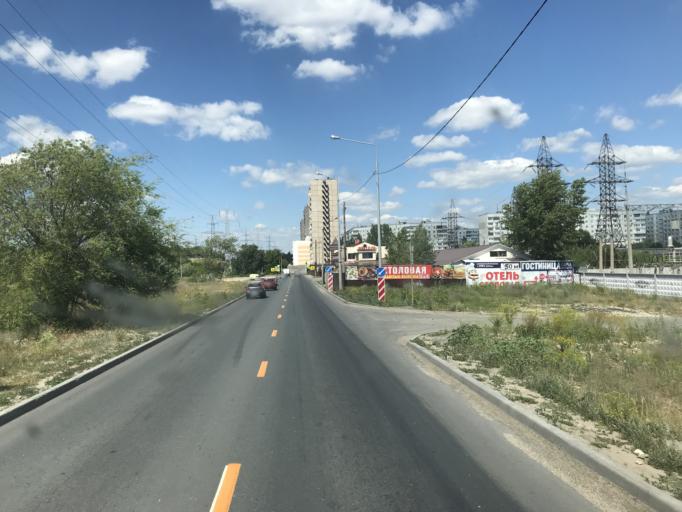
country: RU
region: Samara
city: Zhigulevsk
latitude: 53.4688
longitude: 49.5129
